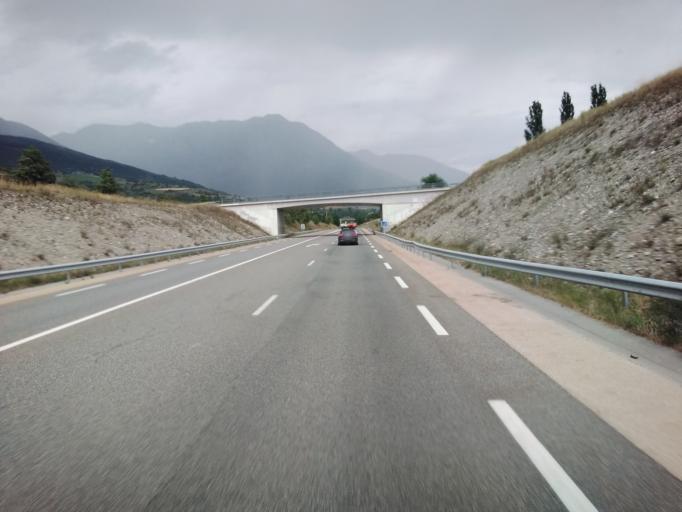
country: FR
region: Provence-Alpes-Cote d'Azur
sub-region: Departement des Hautes-Alpes
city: Embrun
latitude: 44.5789
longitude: 6.5114
